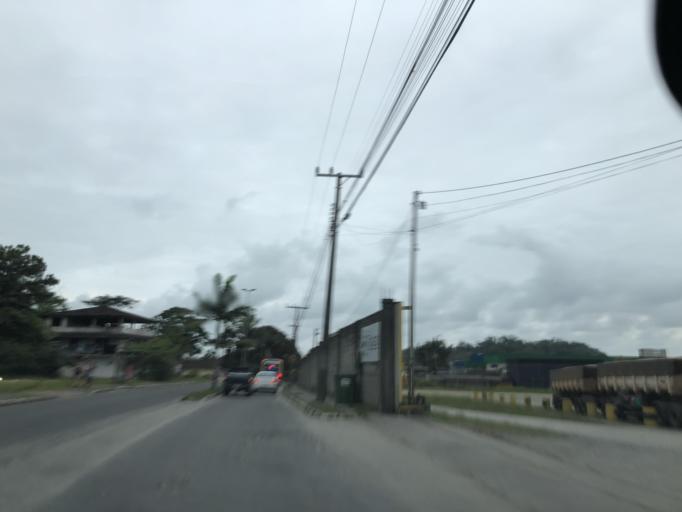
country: BR
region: Santa Catarina
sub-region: Sao Francisco Do Sul
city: Sao Francisco do Sul
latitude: -26.2505
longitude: -48.6206
